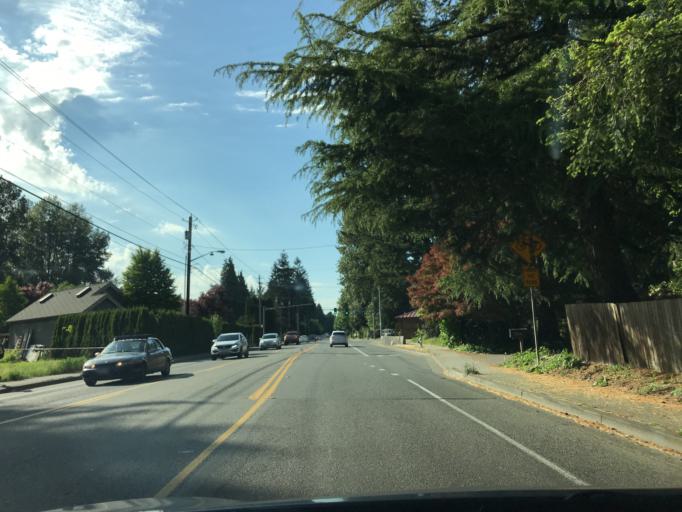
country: US
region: Washington
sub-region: King County
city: Issaquah
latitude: 47.5180
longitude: -122.0290
